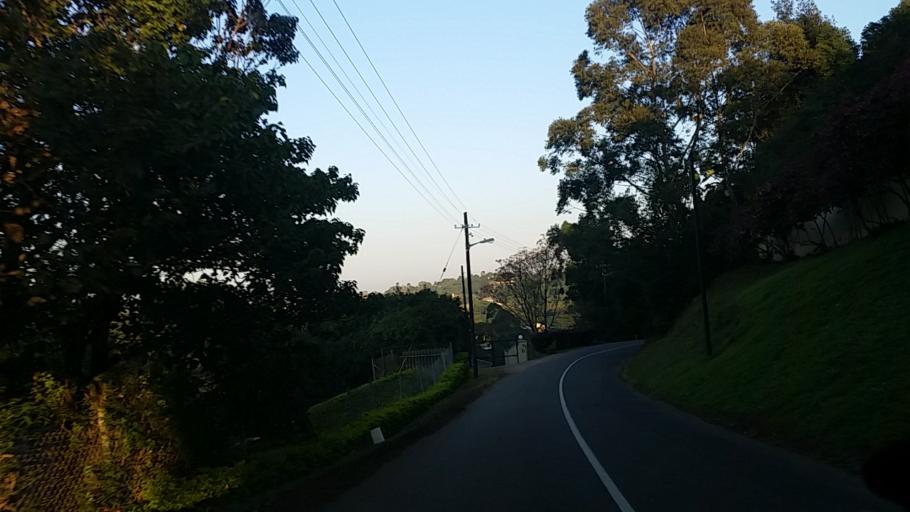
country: ZA
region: KwaZulu-Natal
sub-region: eThekwini Metropolitan Municipality
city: Berea
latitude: -29.8466
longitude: 30.9104
